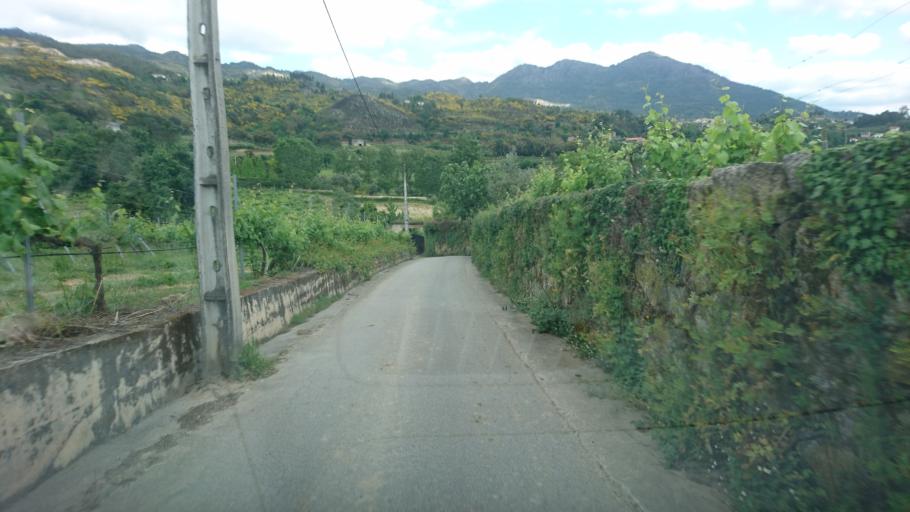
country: PT
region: Vila Real
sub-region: Mondim de Basto
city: Mondim de Basto
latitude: 41.4540
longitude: -7.9291
